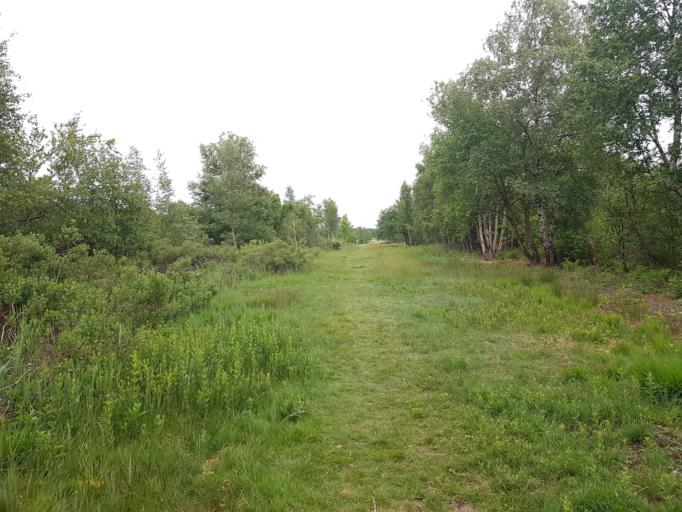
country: NL
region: Friesland
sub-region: Gemeente Boarnsterhim
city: Warten
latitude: 53.1389
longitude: 5.9379
